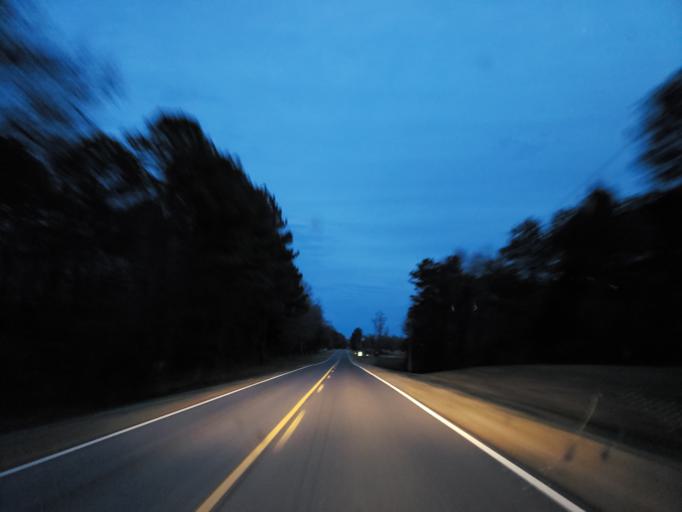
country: US
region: Alabama
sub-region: Greene County
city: Eutaw
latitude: 32.8918
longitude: -87.9507
